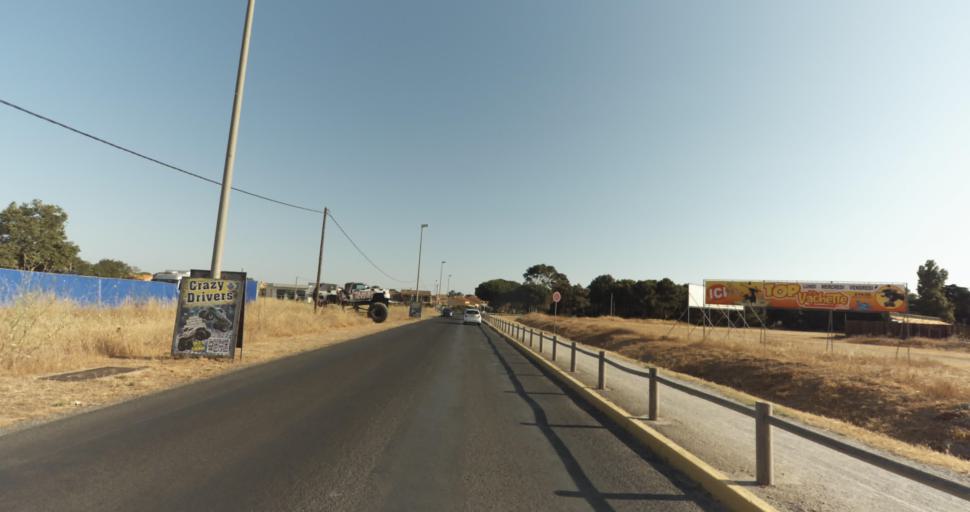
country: FR
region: Languedoc-Roussillon
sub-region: Departement des Pyrenees-Orientales
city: Saint-Cyprien-Plage
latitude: 42.6169
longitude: 3.0332
